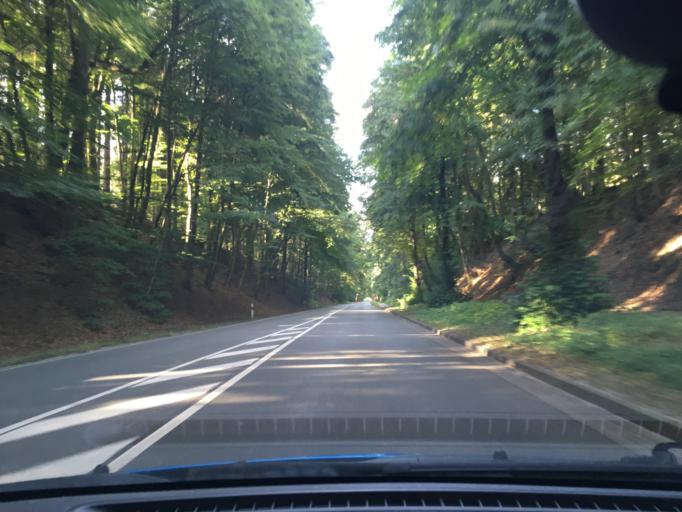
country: DE
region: Lower Saxony
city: Seevetal
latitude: 53.4132
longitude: 9.9274
